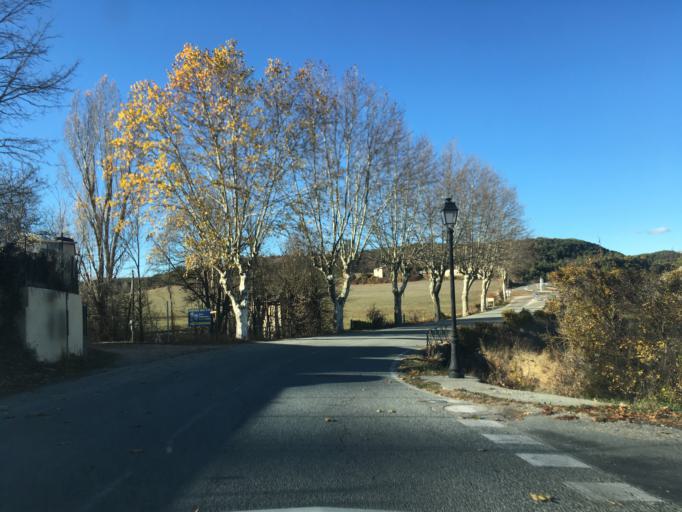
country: FR
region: Provence-Alpes-Cote d'Azur
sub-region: Departement du Var
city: Bargemon
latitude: 43.7111
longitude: 6.5063
